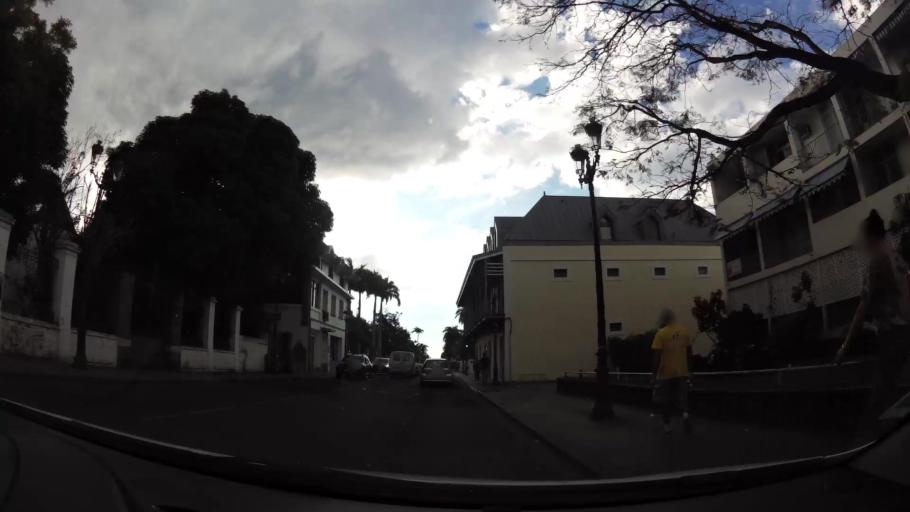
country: RE
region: Reunion
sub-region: Reunion
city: Saint-Denis
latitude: -20.8844
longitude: 55.4506
